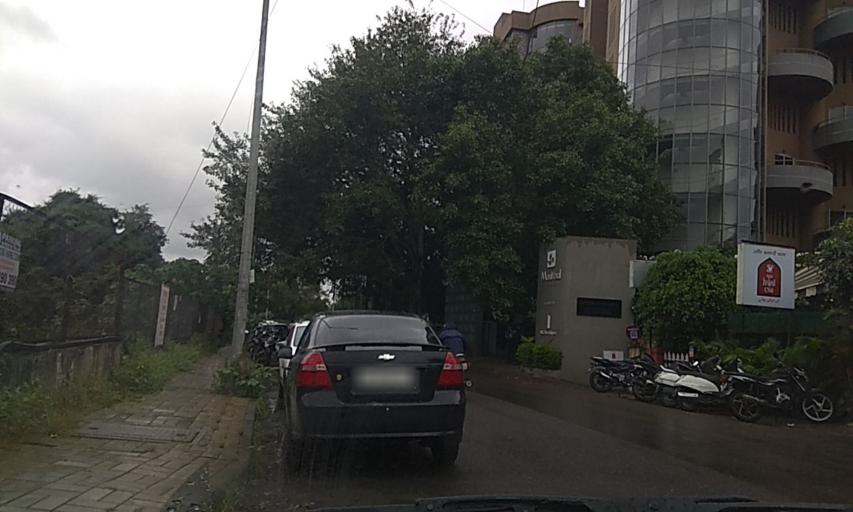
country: IN
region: Maharashtra
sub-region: Pune Division
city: Khadki
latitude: 18.5562
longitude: 73.7993
